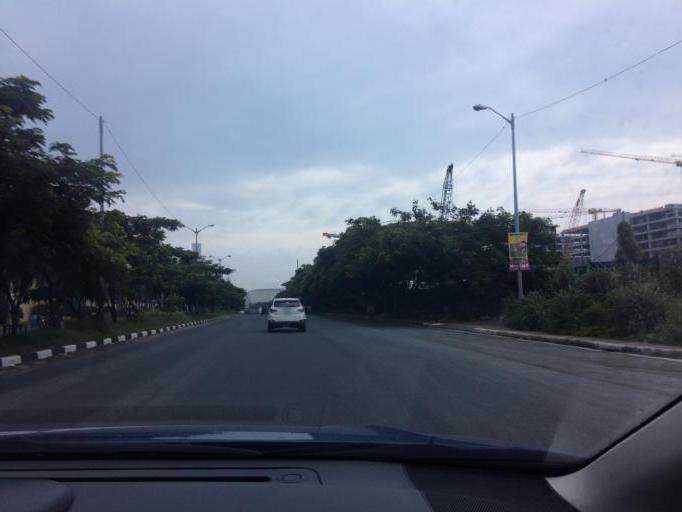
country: PH
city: Sambayanihan People's Village
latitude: 14.5085
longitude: 120.9888
